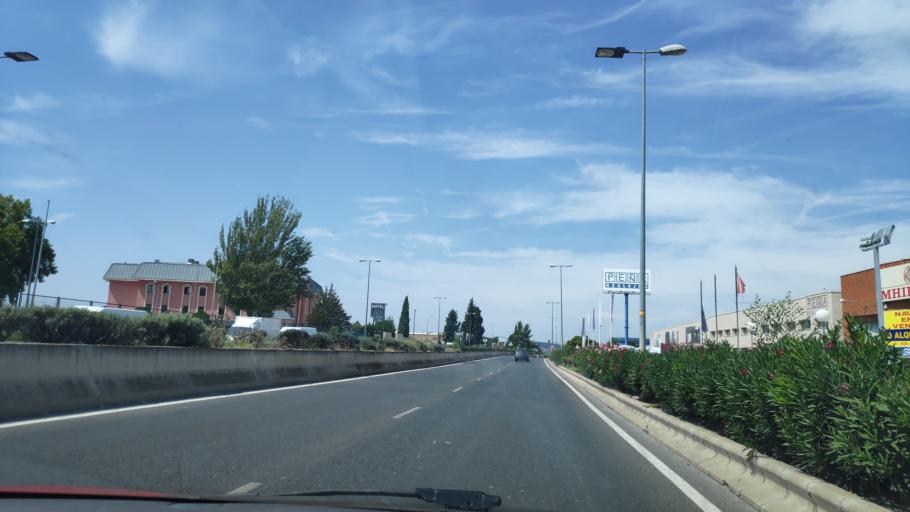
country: ES
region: Madrid
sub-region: Provincia de Madrid
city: Arganda
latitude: 40.3068
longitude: -3.4663
